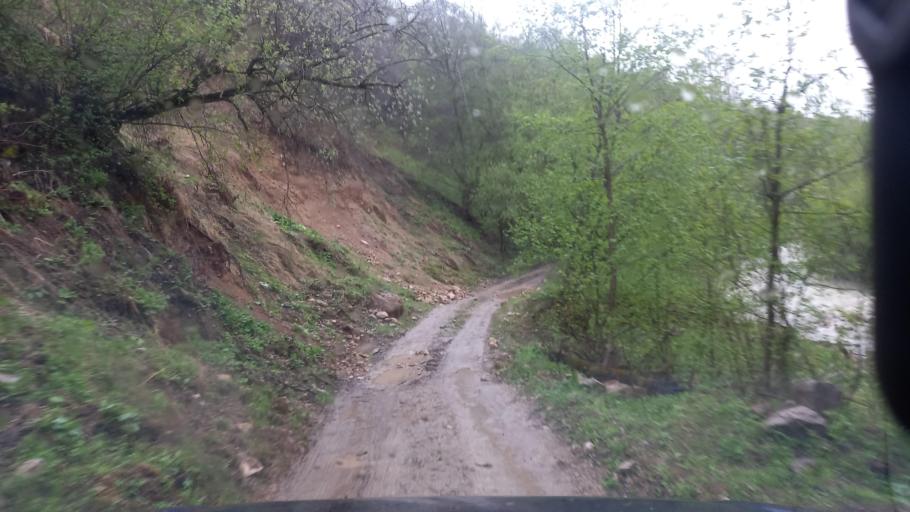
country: RU
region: Kabardino-Balkariya
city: Bylym
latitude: 43.5997
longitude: 42.9230
